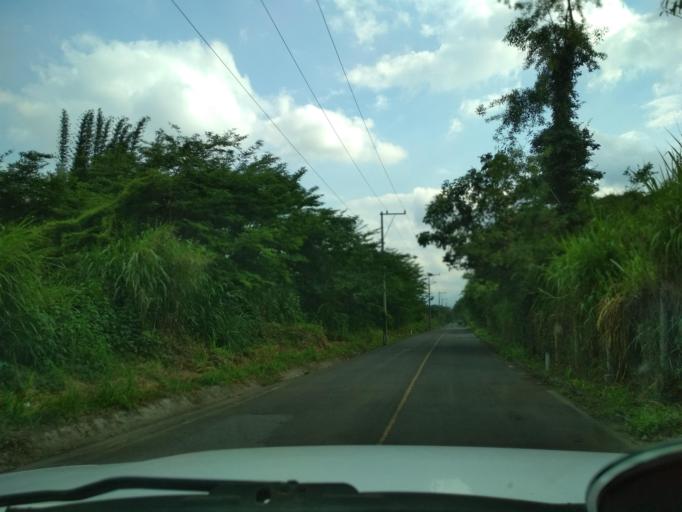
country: MX
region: Veracruz
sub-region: Ixtaczoquitlan
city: Buenavista
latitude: 18.9118
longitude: -97.0267
